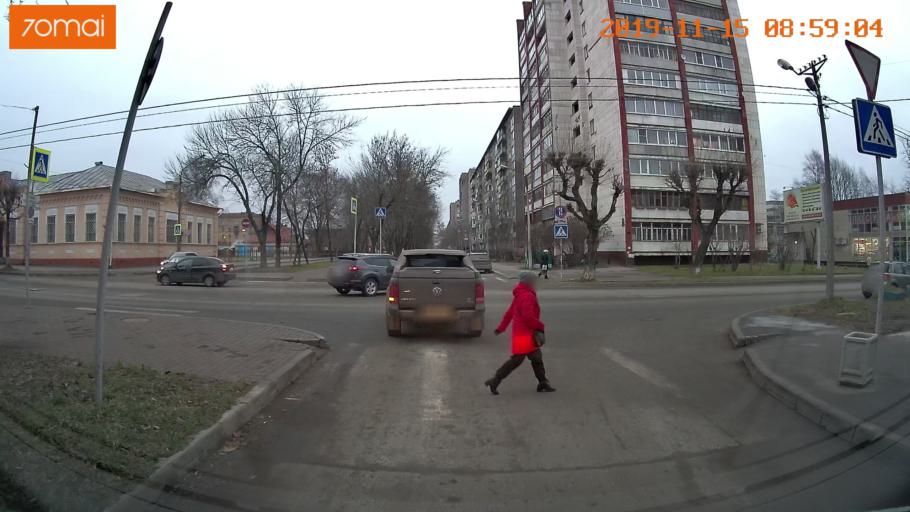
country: RU
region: Vologda
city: Cherepovets
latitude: 59.1282
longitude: 37.9240
